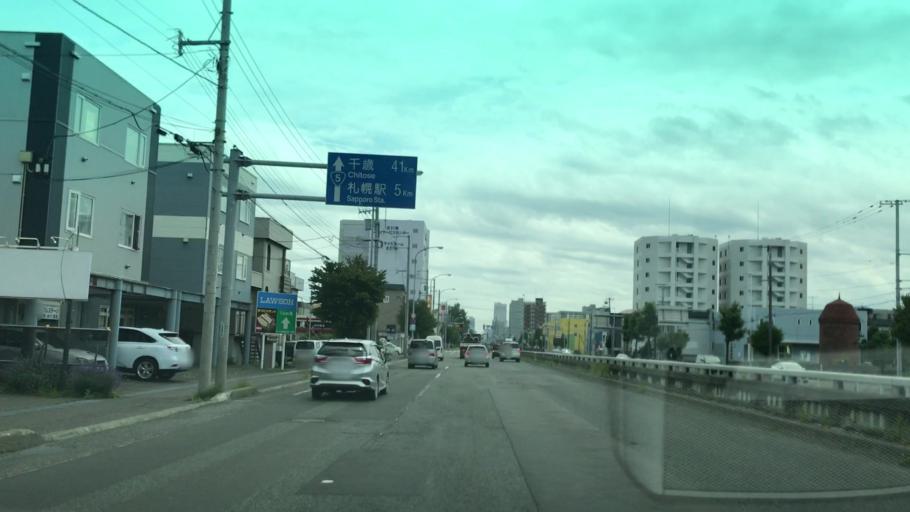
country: JP
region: Hokkaido
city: Sapporo
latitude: 43.0997
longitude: 141.3455
